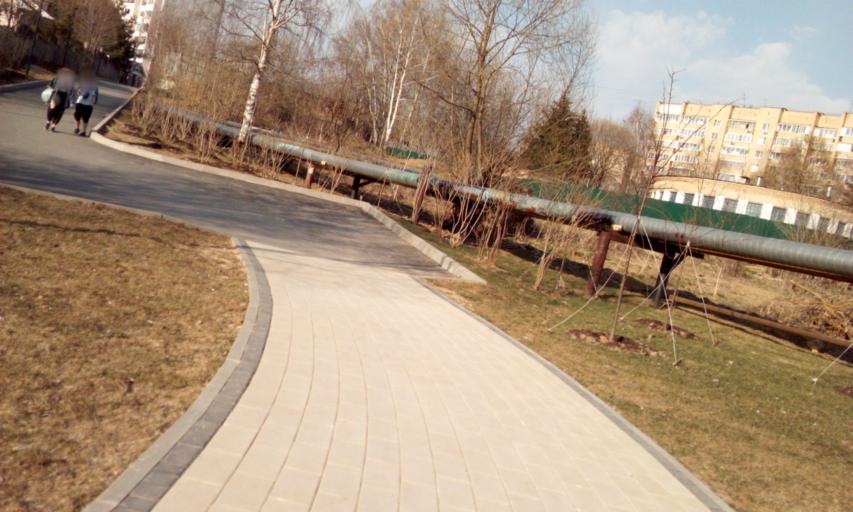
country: RU
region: Moskovskaya
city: Kommunarka
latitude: 55.5293
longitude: 37.4405
